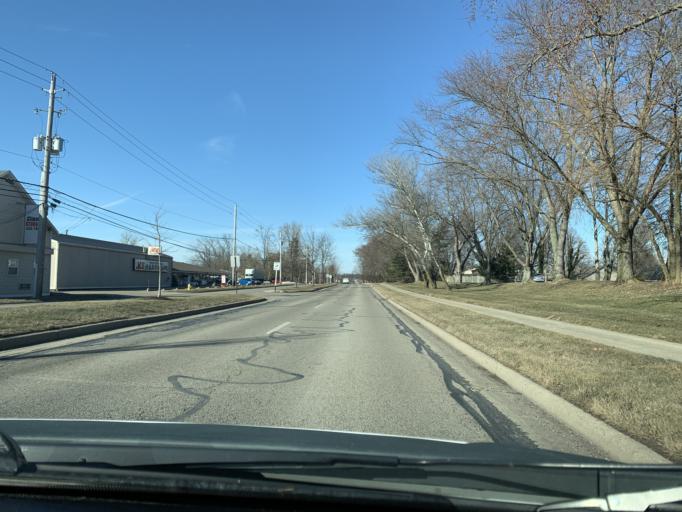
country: US
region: Ohio
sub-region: Montgomery County
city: Centerville
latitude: 39.6303
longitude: -84.1392
